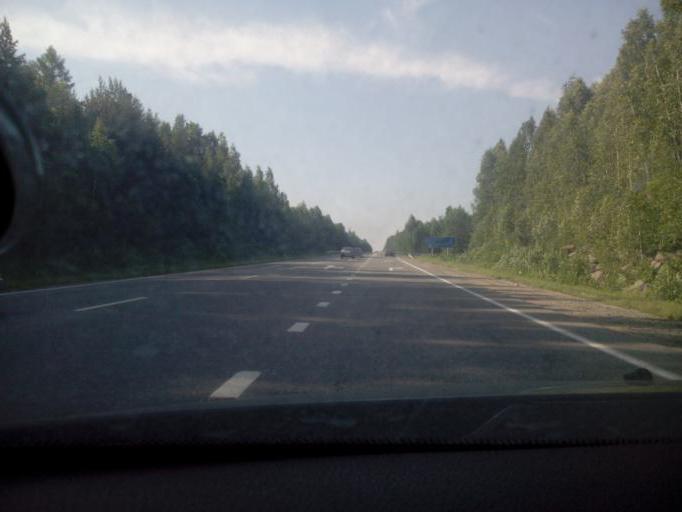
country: RU
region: Sverdlovsk
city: Verkh-Neyvinskiy
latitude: 57.3062
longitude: 60.2917
